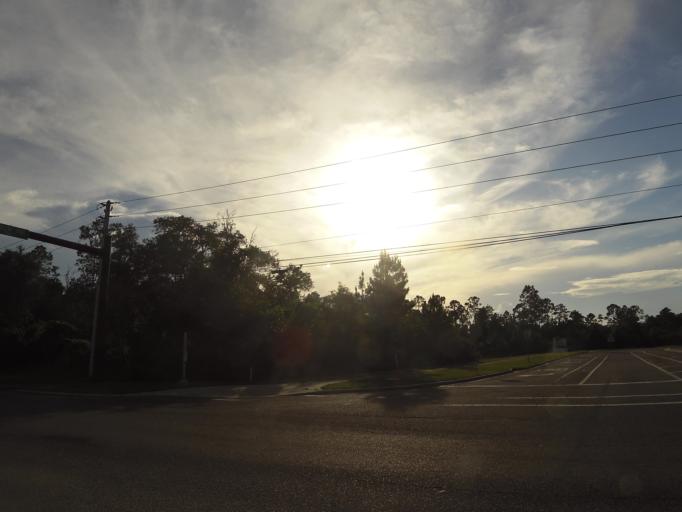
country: US
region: Florida
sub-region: Clay County
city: Green Cove Springs
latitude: 30.0150
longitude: -81.6056
